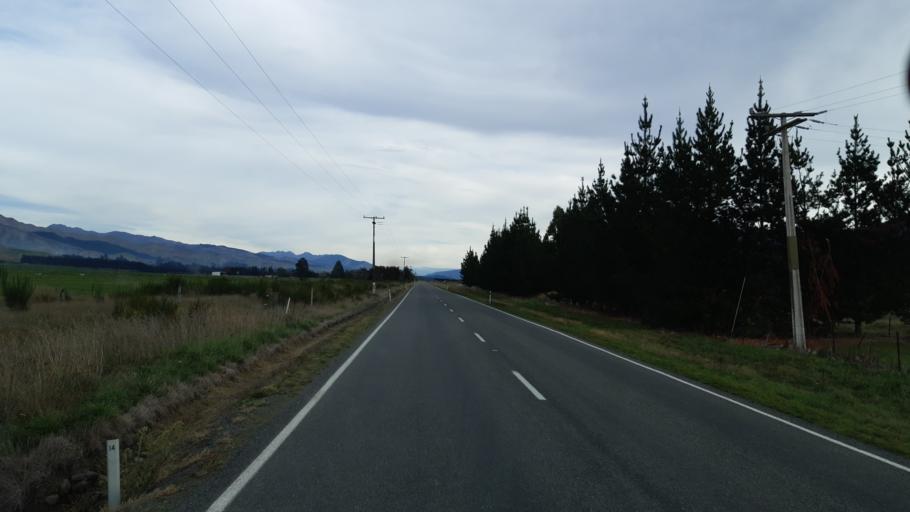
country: NZ
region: Tasman
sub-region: Tasman District
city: Richmond
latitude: -41.6047
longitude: 173.4131
